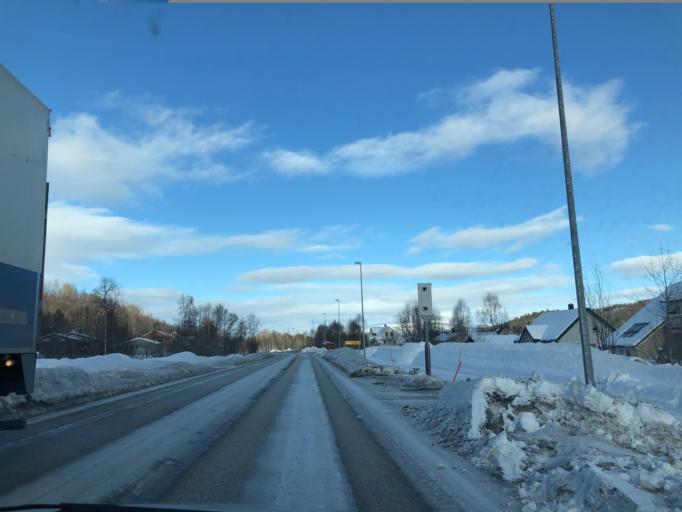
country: NO
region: Troms
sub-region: Malselv
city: Moen
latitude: 69.0326
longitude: 18.5040
